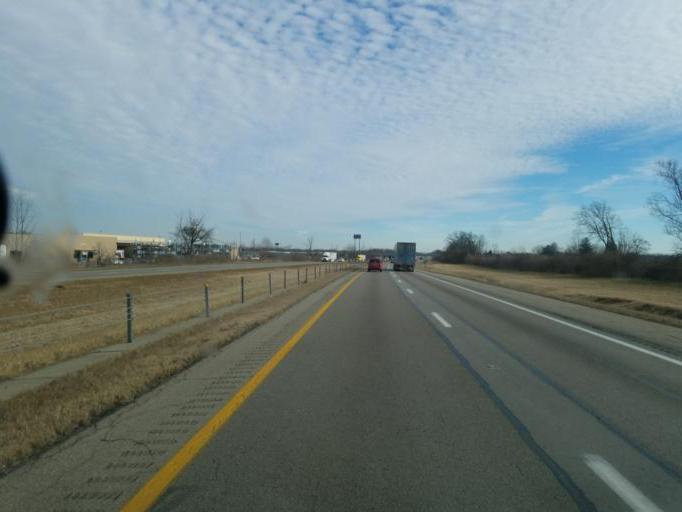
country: US
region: Ohio
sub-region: Montgomery County
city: Clayton
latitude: 39.8548
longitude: -84.3368
